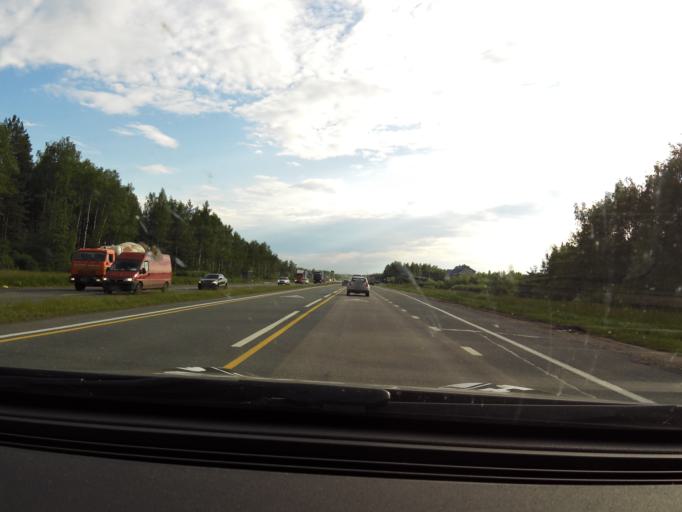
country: RU
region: Vladimir
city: Sudogda
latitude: 56.1365
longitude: 40.8896
